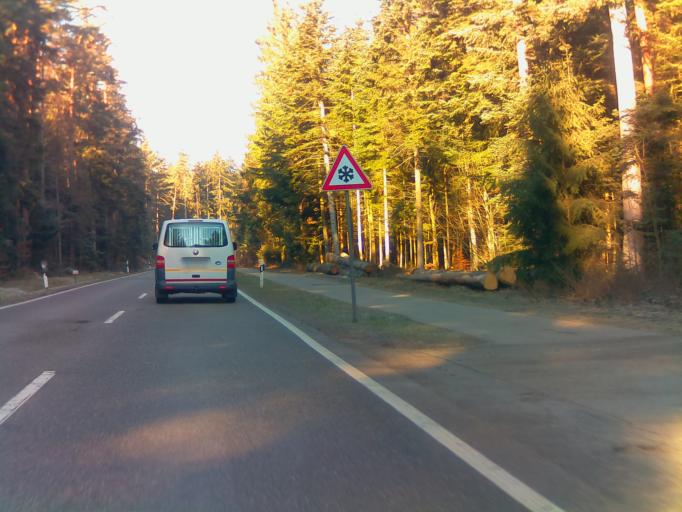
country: DE
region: Baden-Wuerttemberg
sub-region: Karlsruhe Region
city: Oberreichenbach
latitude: 48.7269
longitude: 8.6606
